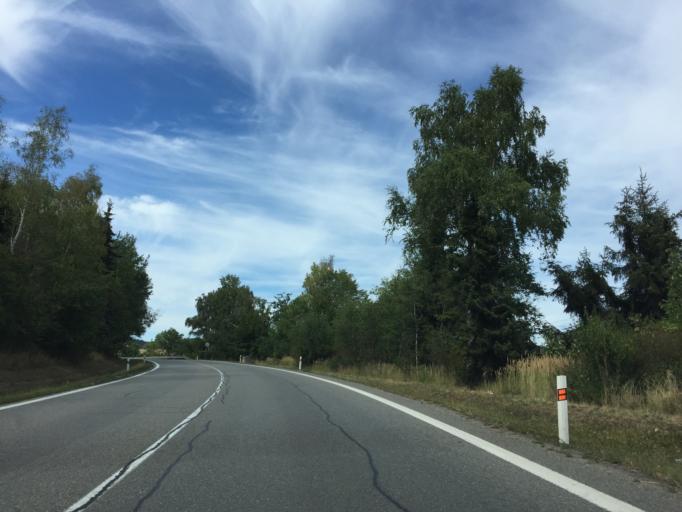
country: CZ
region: Jihocesky
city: Chotoviny
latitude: 49.5547
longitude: 14.6663
